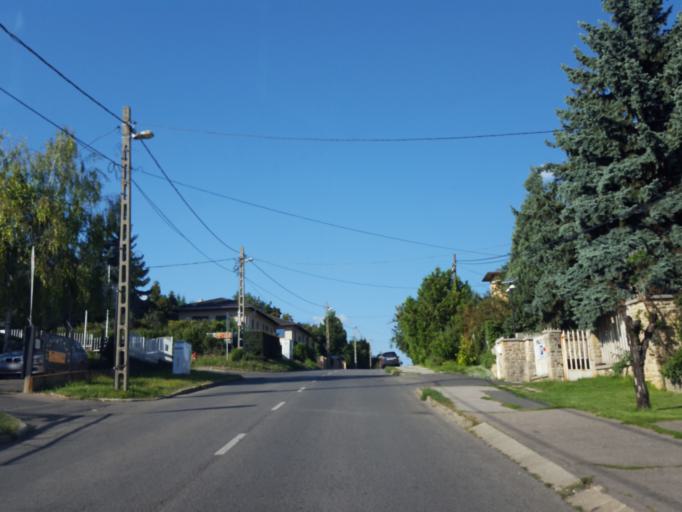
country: HU
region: Budapest
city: Budapest XXII. keruelet
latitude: 47.4453
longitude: 19.0130
